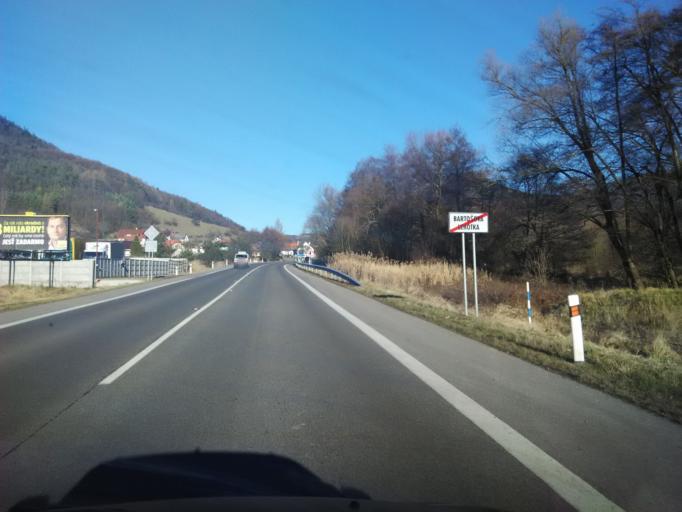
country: SK
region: Banskobystricky
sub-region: Okres Ziar nad Hronom
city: Kremnica
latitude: 48.6596
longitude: 18.9108
